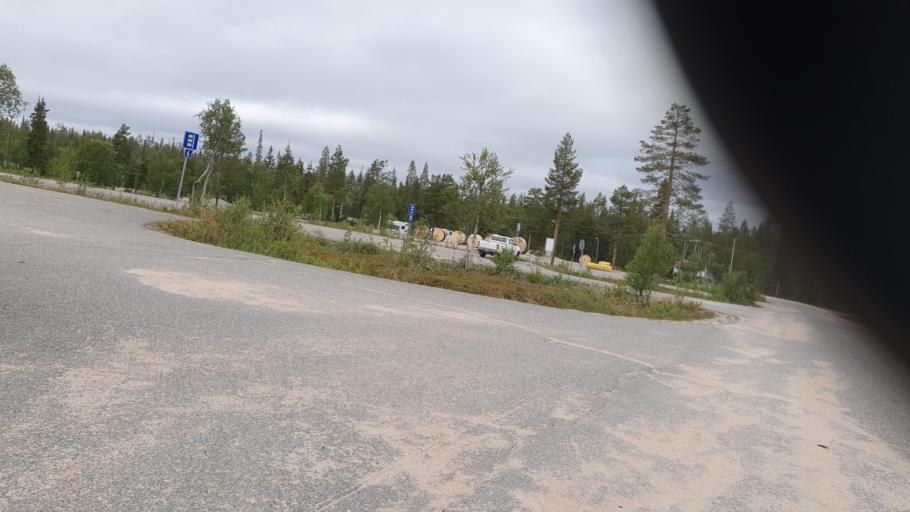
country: FI
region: Lapland
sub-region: Tunturi-Lappi
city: Kolari
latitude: 67.5822
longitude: 24.2058
